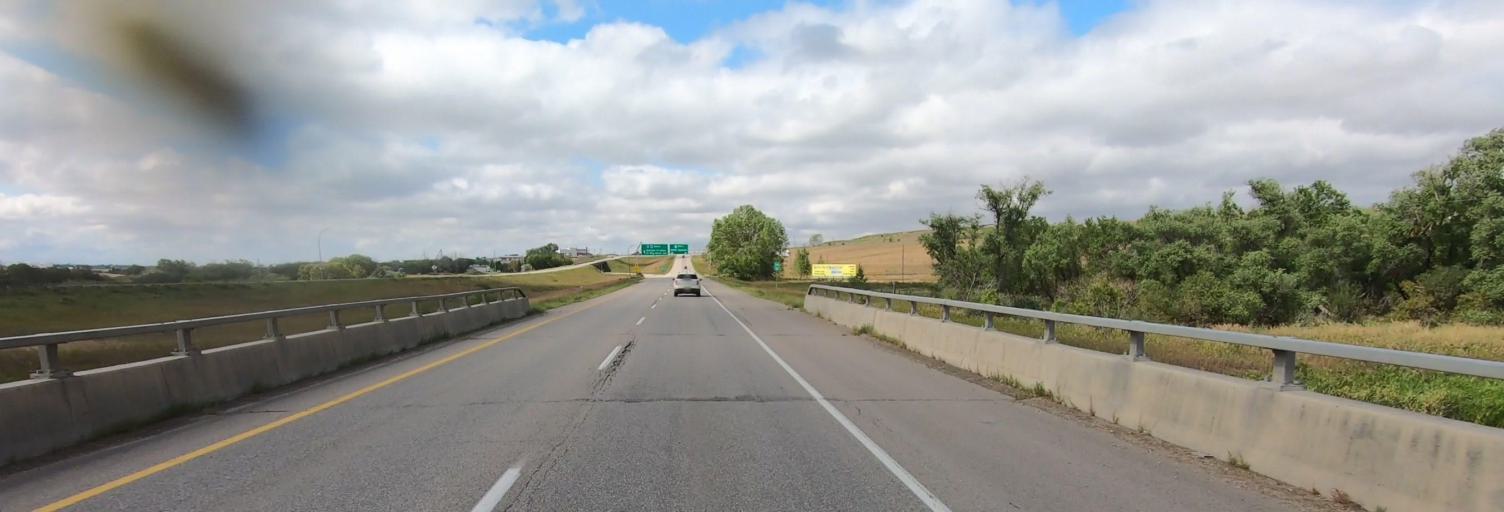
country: CA
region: Saskatchewan
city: Moose Jaw
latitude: 50.3950
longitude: -105.4755
